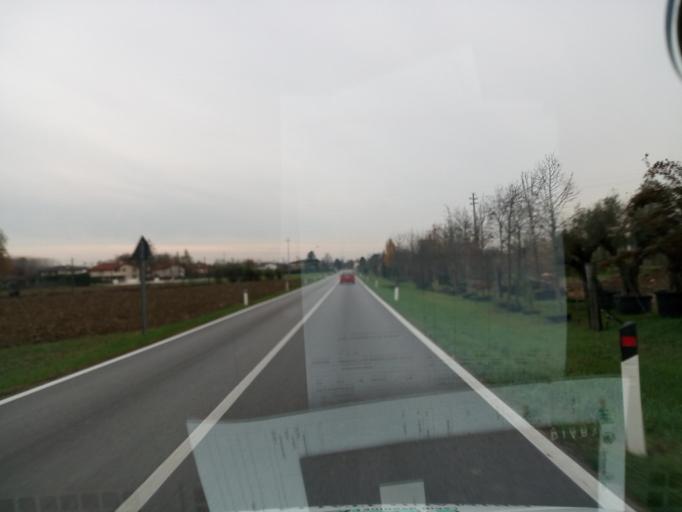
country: IT
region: Veneto
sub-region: Provincia di Padova
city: Piombino Dese
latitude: 45.5895
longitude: 12.0019
